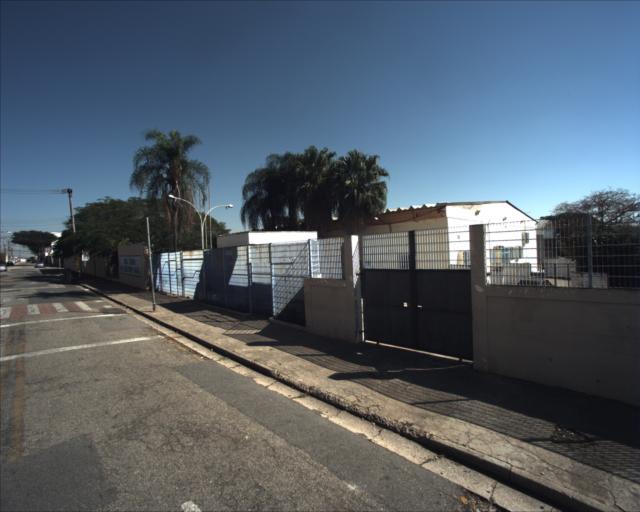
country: BR
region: Sao Paulo
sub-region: Sorocaba
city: Sorocaba
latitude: -23.4933
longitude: -47.4382
